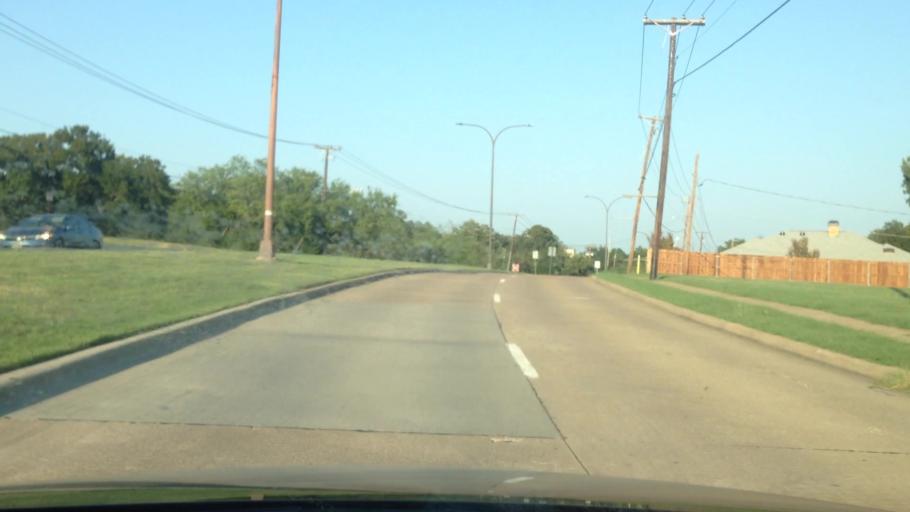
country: US
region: Texas
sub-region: Tarrant County
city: Dalworthington Gardens
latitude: 32.6822
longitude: -97.1902
